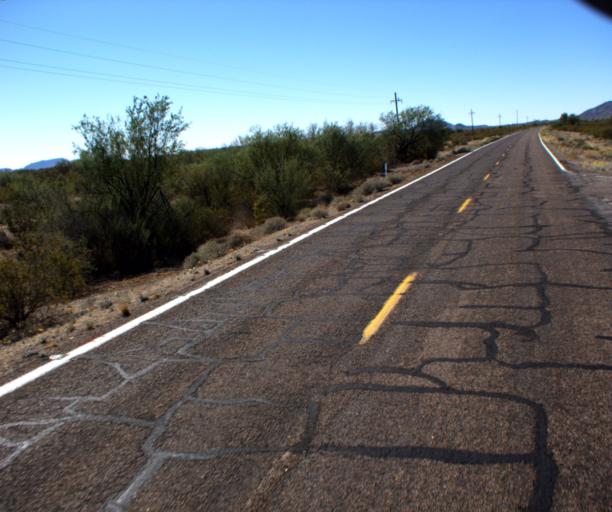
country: US
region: Arizona
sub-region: Pima County
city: Ajo
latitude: 32.4475
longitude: -112.8711
